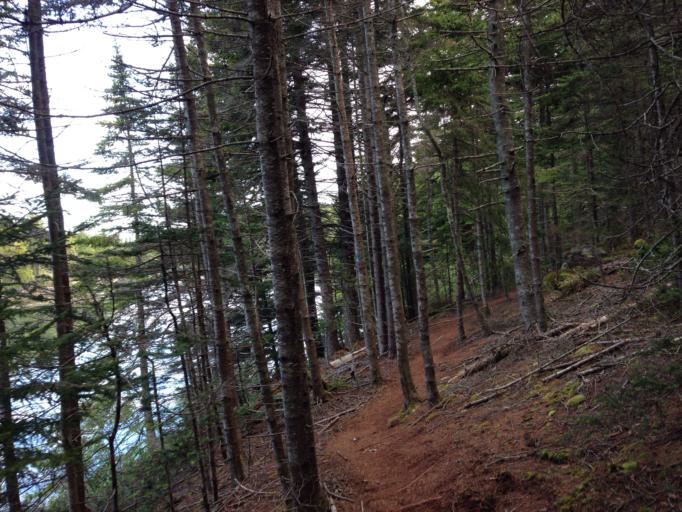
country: US
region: Maine
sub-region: Hancock County
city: Gouldsboro
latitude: 44.3811
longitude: -68.0717
